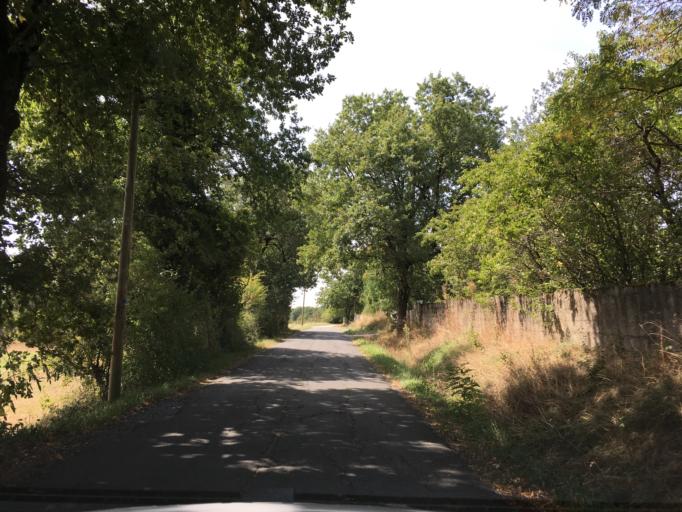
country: FR
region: Midi-Pyrenees
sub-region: Departement du Tarn
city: Castres
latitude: 43.6492
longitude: 2.2340
